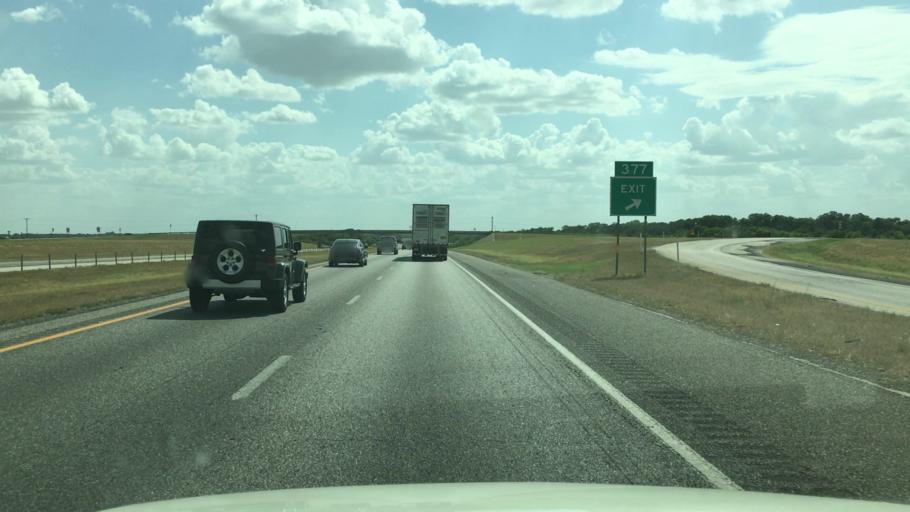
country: US
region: Texas
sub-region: Ellis County
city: Plum Grove
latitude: 32.1064
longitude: -97.0072
